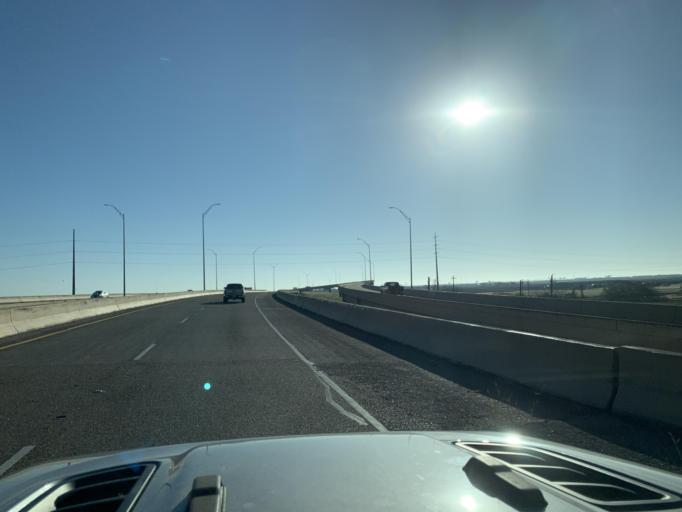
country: US
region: Texas
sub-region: Nueces County
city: Corpus Christi
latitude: 27.7848
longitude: -97.4878
